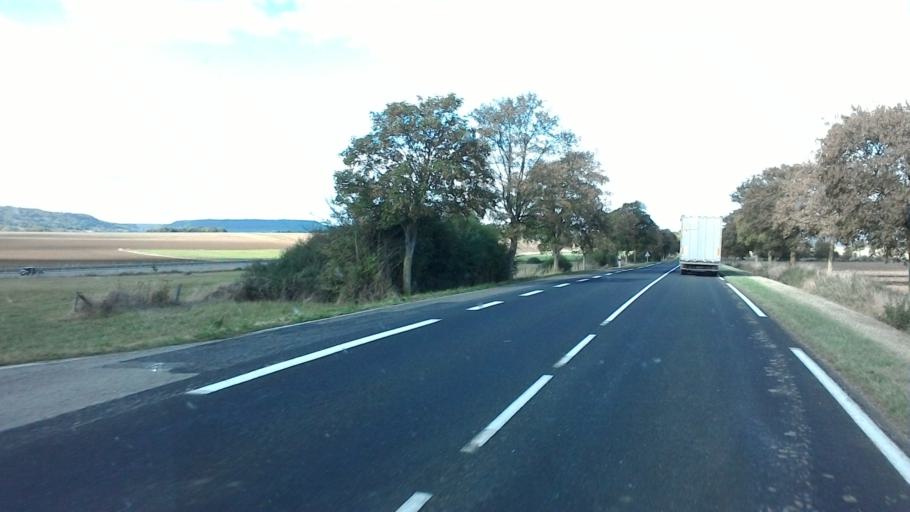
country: FR
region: Lorraine
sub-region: Departement de Meurthe-et-Moselle
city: Colombey-les-Belles
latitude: 48.5674
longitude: 5.8895
